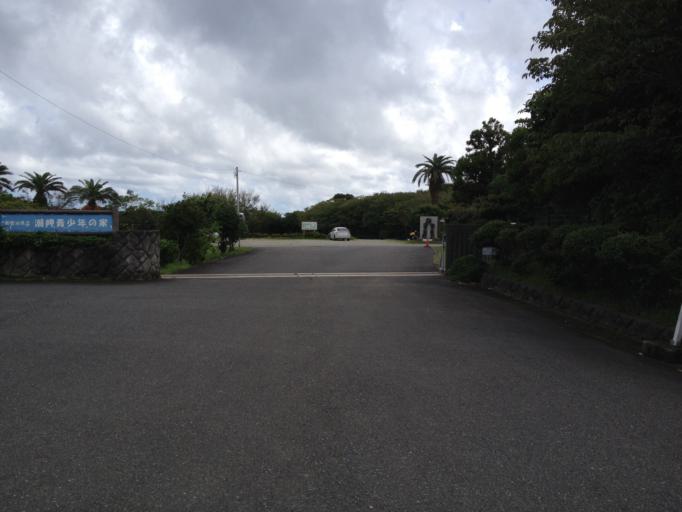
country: JP
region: Wakayama
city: Shingu
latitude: 33.4472
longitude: 135.7818
